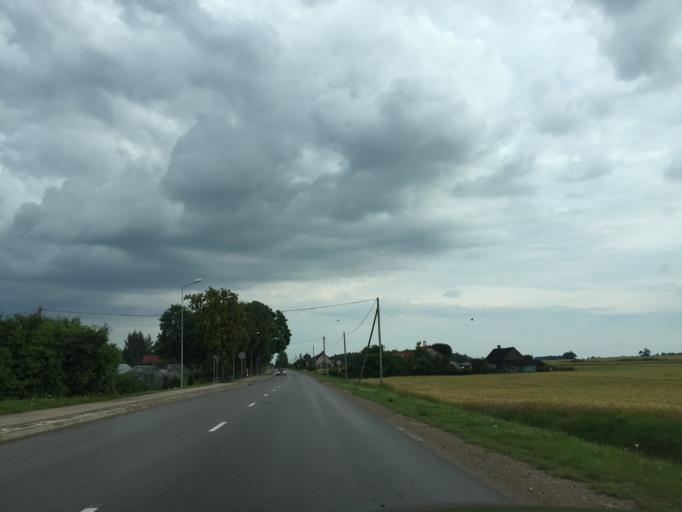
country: LV
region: Dobeles Rajons
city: Dobele
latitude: 56.6096
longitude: 23.2744
